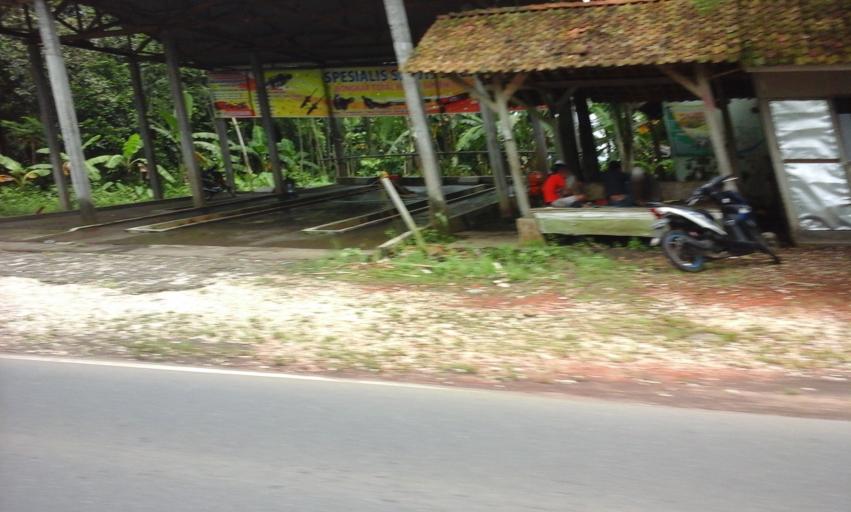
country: ID
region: East Java
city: Jatiroto
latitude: -8.1253
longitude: 113.3752
